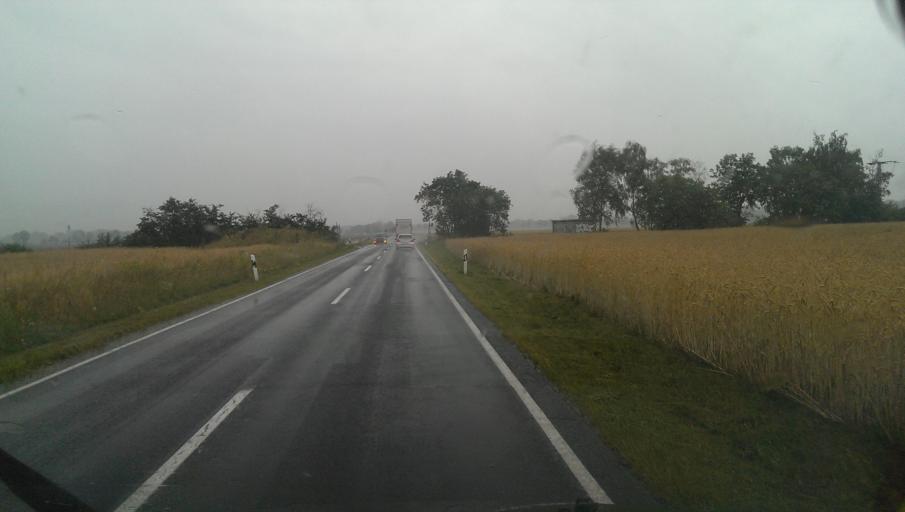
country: DE
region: Brandenburg
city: Roskow
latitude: 52.4722
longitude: 12.6917
